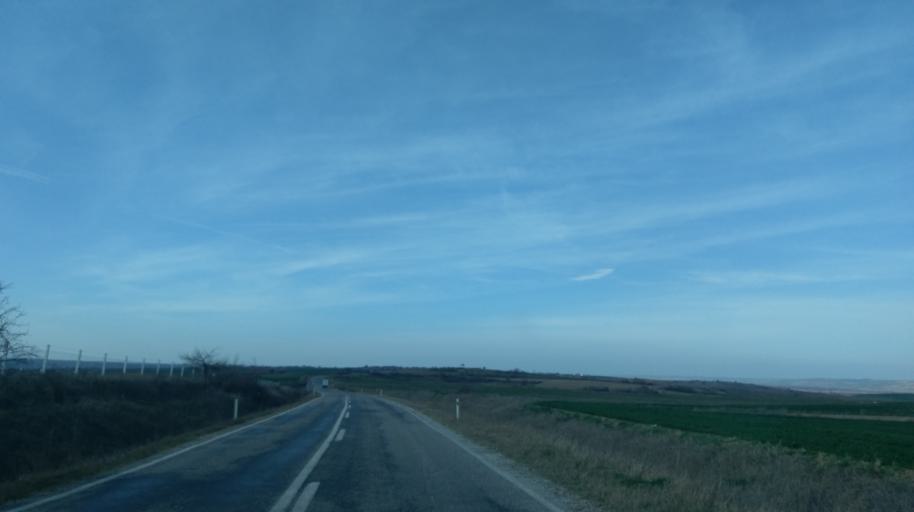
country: TR
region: Kirklareli
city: Pehlivankoy
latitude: 41.3213
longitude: 26.8716
